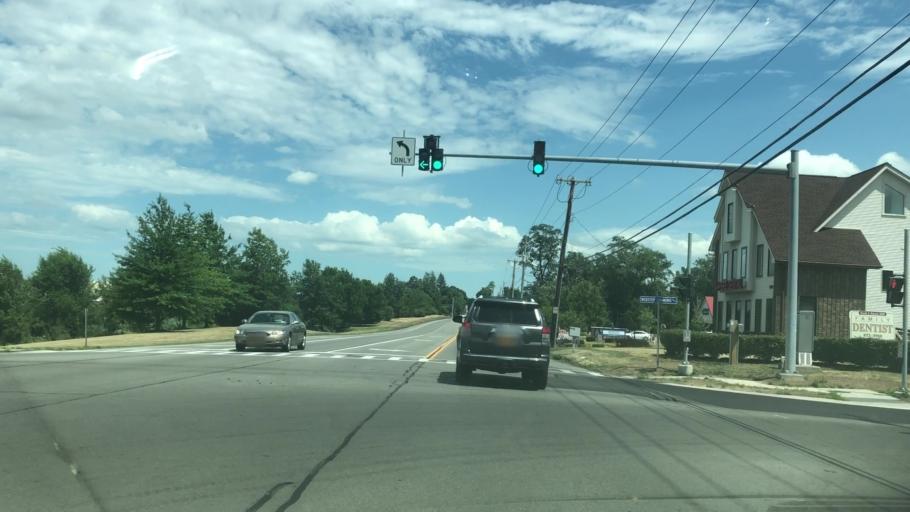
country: US
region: New York
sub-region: Monroe County
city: Webster
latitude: 43.2098
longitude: -77.4519
